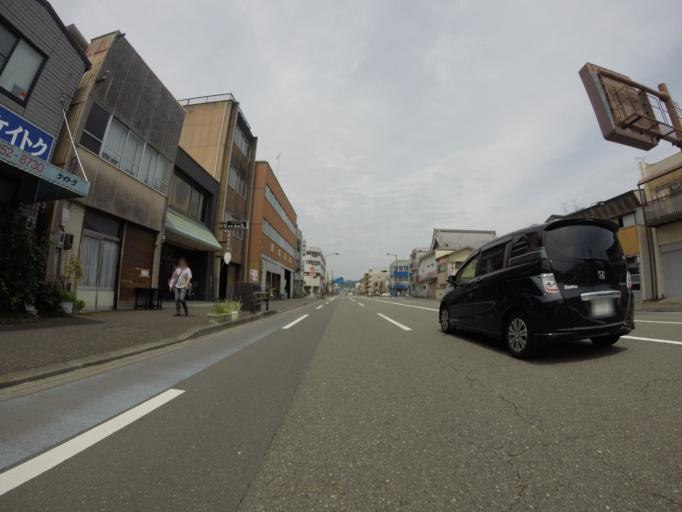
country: JP
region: Shizuoka
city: Shizuoka-shi
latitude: 34.9755
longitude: 138.3727
